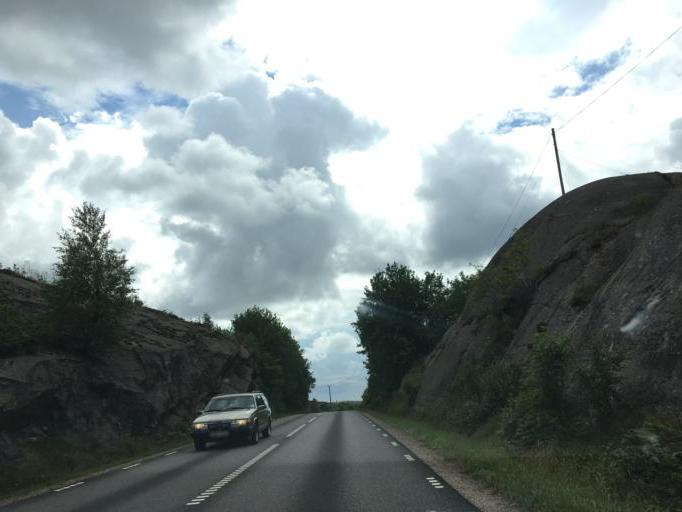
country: SE
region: Vaestra Goetaland
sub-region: Sotenas Kommun
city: Kungshamn
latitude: 58.3997
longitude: 11.2660
